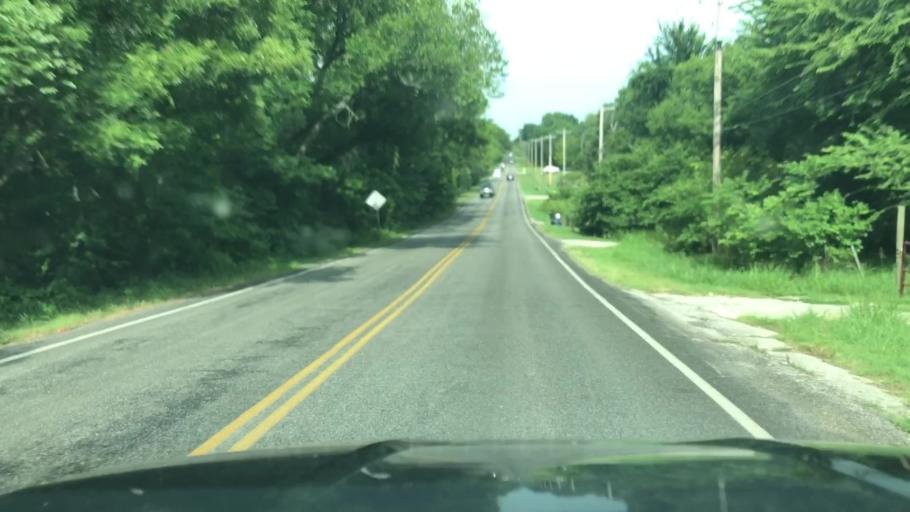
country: US
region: Oklahoma
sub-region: Tulsa County
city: Oakhurst
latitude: 36.0902
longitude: -96.1111
